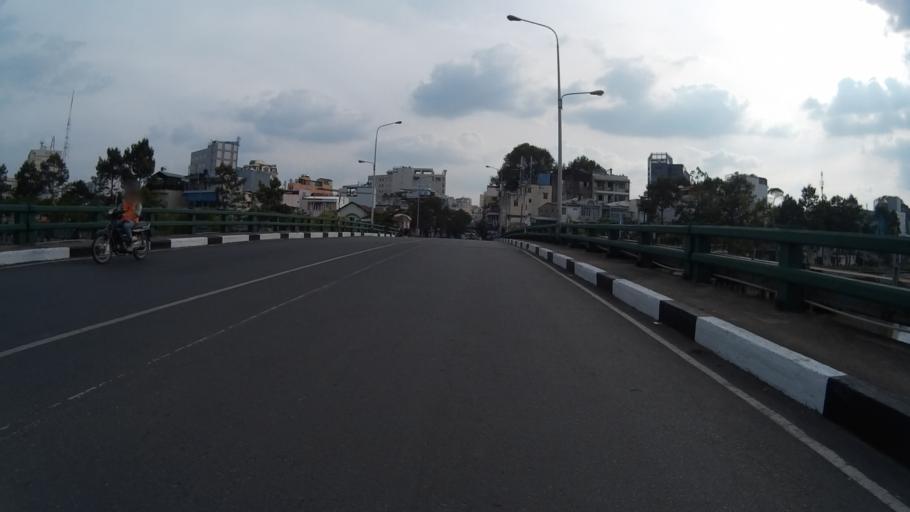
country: VN
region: Ho Chi Minh City
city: Quan Binh Thanh
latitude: 10.7939
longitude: 106.6975
